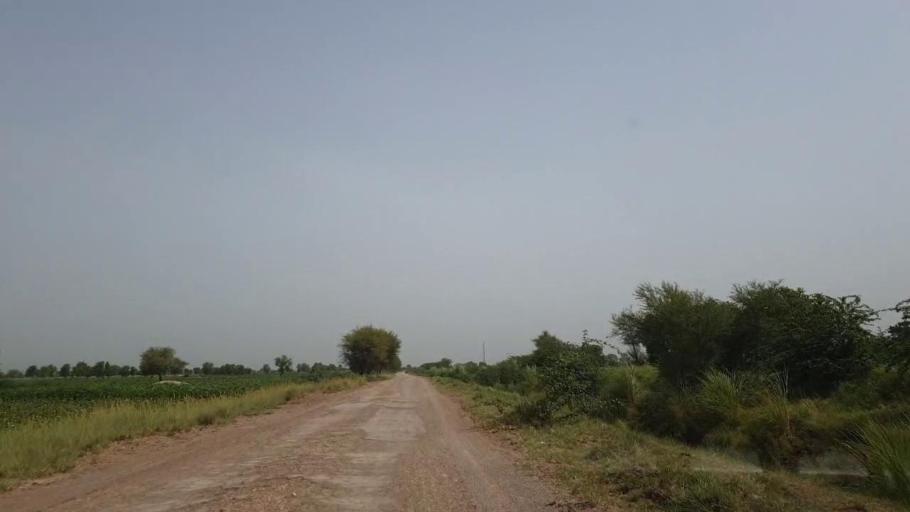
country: PK
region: Sindh
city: Sakrand
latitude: 26.1328
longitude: 68.3643
